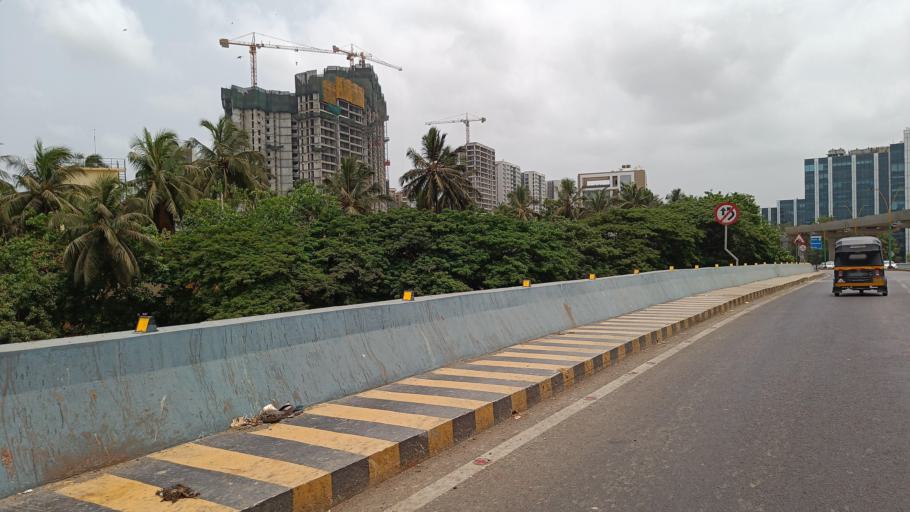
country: IN
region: Maharashtra
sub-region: Mumbai Suburban
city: Mumbai
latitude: 19.0531
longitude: 72.8477
